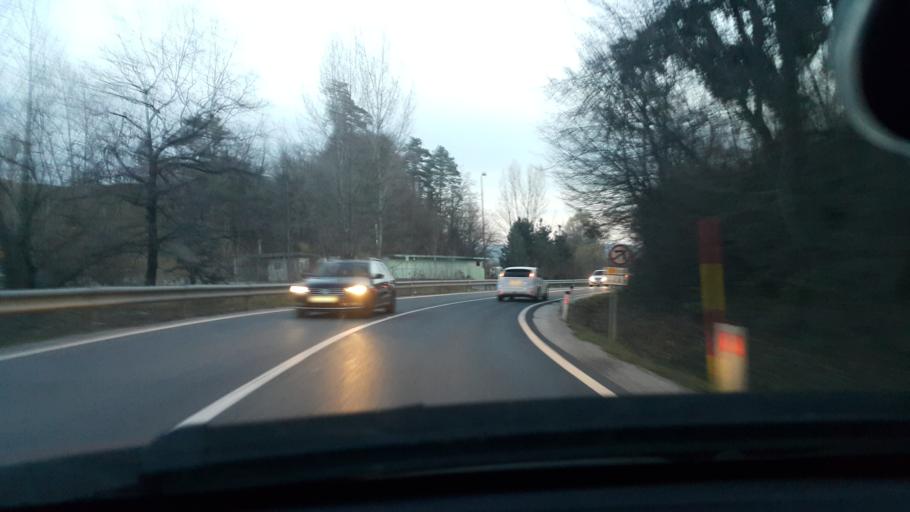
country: SI
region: Zalec
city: Gotovlje
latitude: 46.2913
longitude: 15.1735
